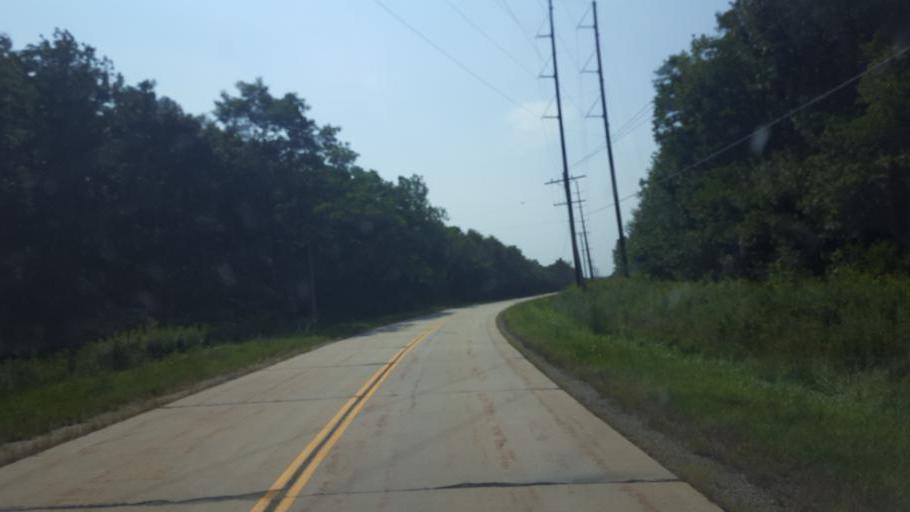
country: US
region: Ohio
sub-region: Lake County
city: Madison
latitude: 41.6696
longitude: -81.0373
